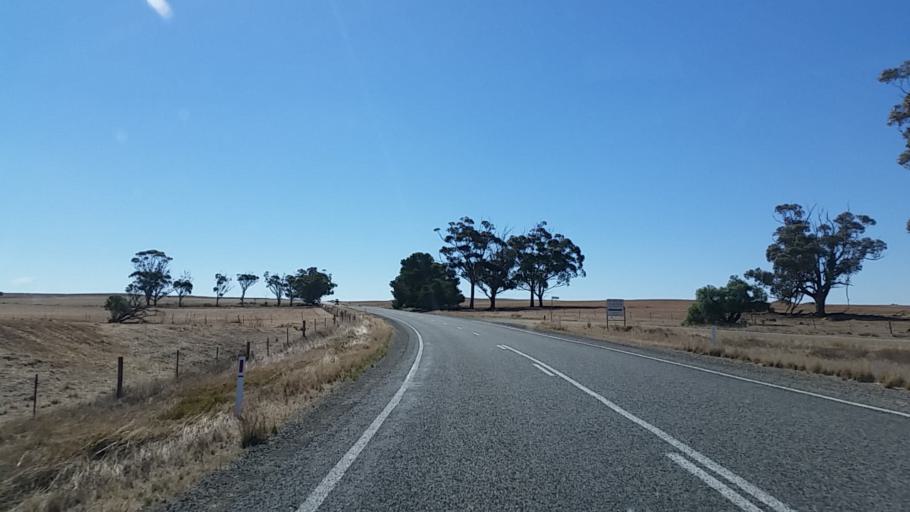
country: AU
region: South Australia
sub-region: Northern Areas
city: Jamestown
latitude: -33.3381
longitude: 138.8928
